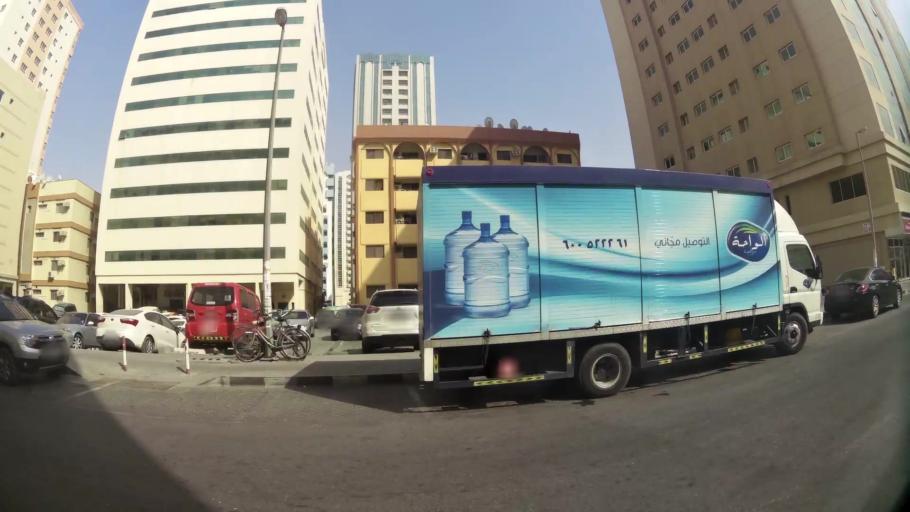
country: AE
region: Ash Shariqah
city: Sharjah
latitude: 25.3386
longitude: 55.3916
